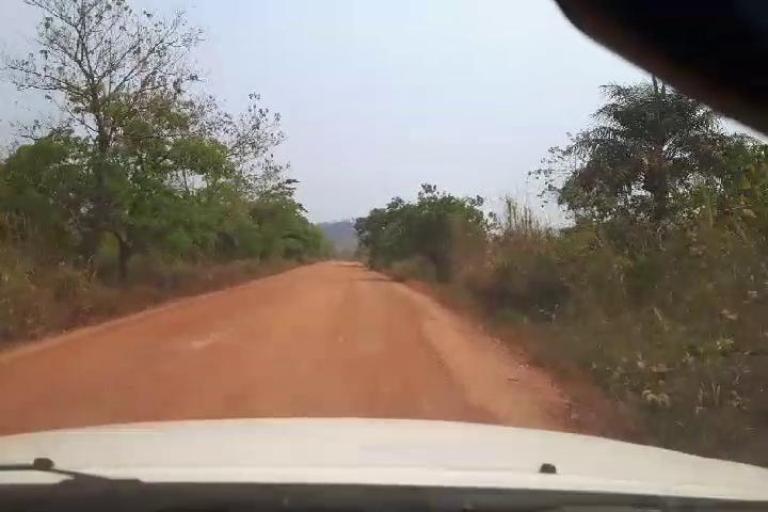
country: SL
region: Northern Province
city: Bumbuna
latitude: 9.0220
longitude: -11.7635
